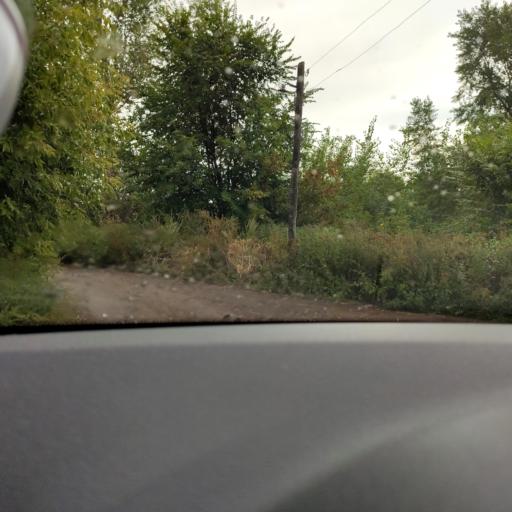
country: RU
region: Samara
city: Samara
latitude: 53.1725
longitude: 50.1579
